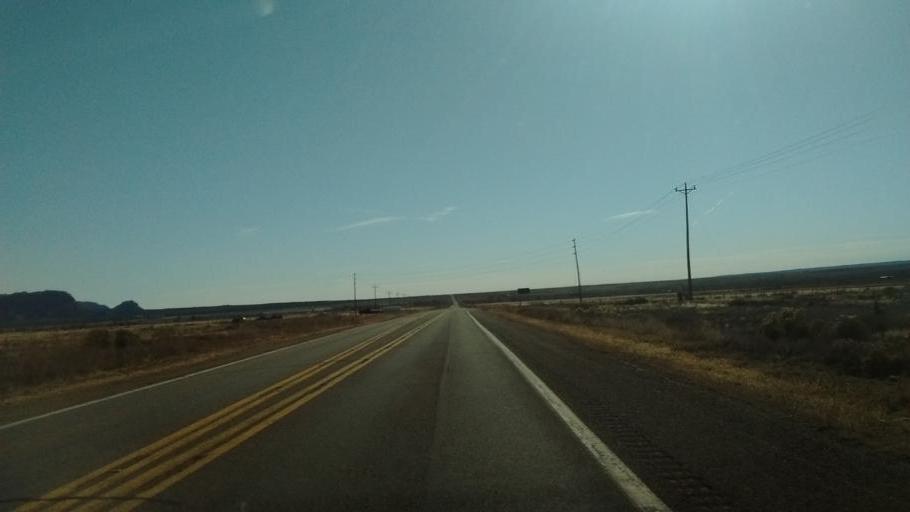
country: US
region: Arizona
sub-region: Mohave County
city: Colorado City
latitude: 36.9486
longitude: -112.9575
